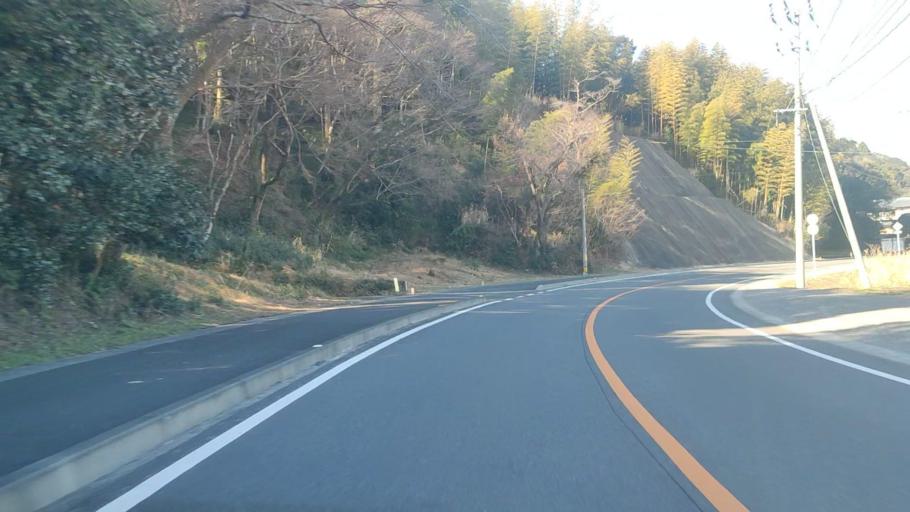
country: JP
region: Oita
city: Saiki
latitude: 32.9258
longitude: 131.9235
